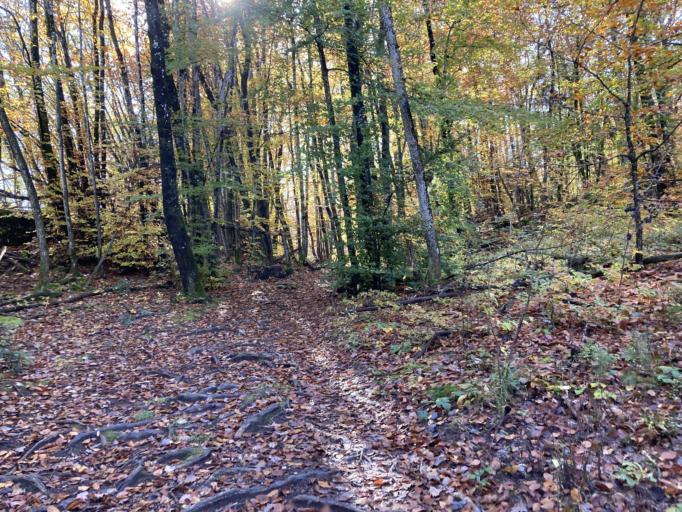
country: FR
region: Rhone-Alpes
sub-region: Departement de la Haute-Savoie
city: Sevrier
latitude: 45.8777
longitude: 6.1345
